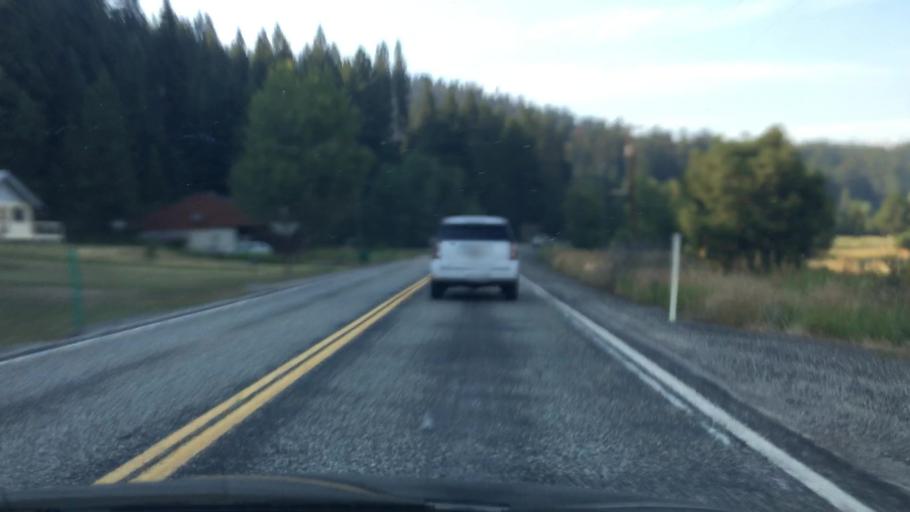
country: US
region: Idaho
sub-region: Valley County
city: Cascade
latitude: 44.3066
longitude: -116.0875
